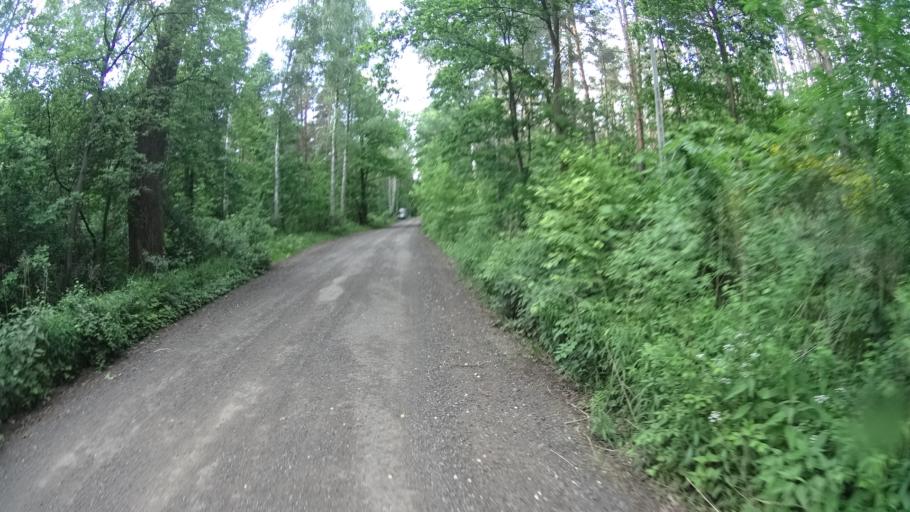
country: PL
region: Masovian Voivodeship
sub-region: Powiat pruszkowski
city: Nadarzyn
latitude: 52.0639
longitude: 20.8210
